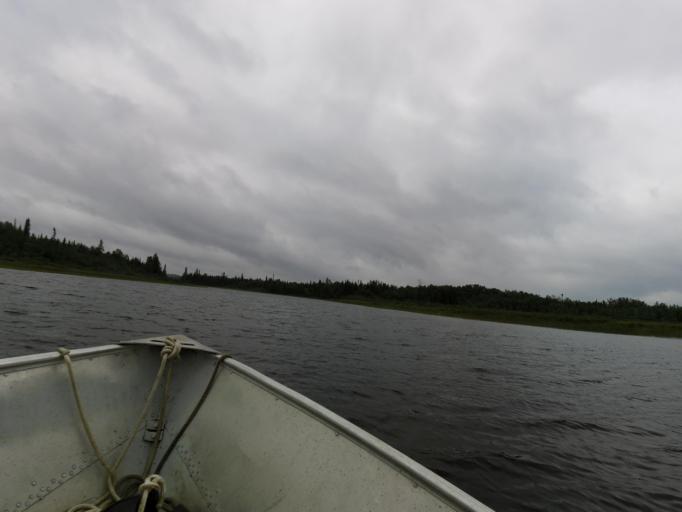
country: CA
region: Ontario
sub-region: Rainy River District
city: Atikokan
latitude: 49.5977
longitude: -91.3413
